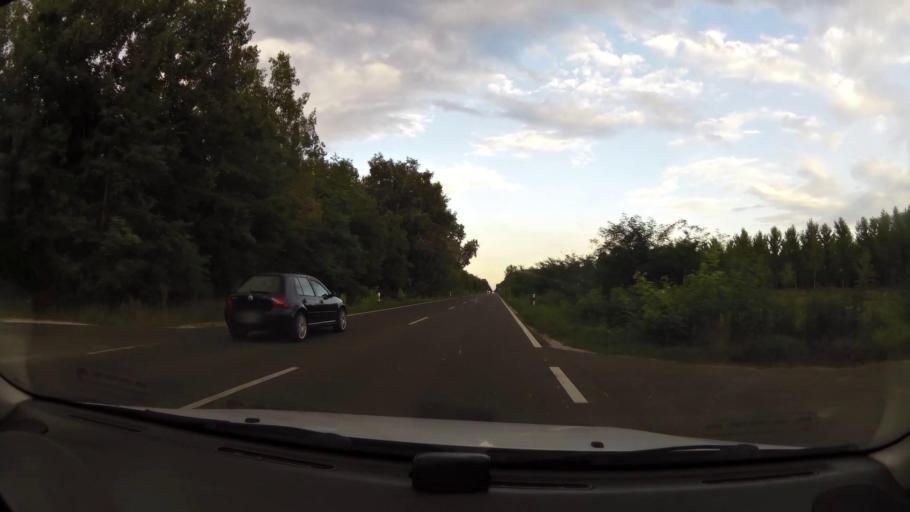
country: HU
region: Pest
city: Ujszilvas
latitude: 47.2971
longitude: 19.8953
